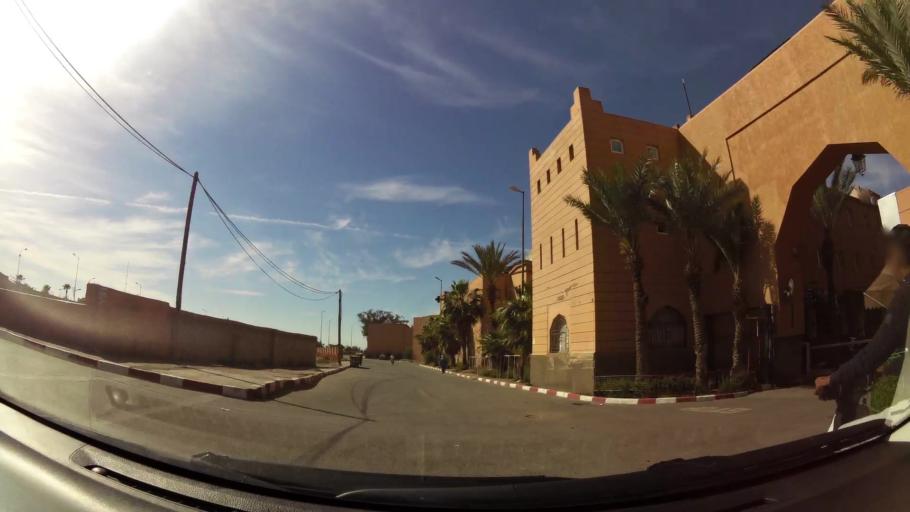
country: MA
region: Marrakech-Tensift-Al Haouz
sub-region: Marrakech
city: Marrakesh
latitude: 31.6389
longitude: -7.9803
